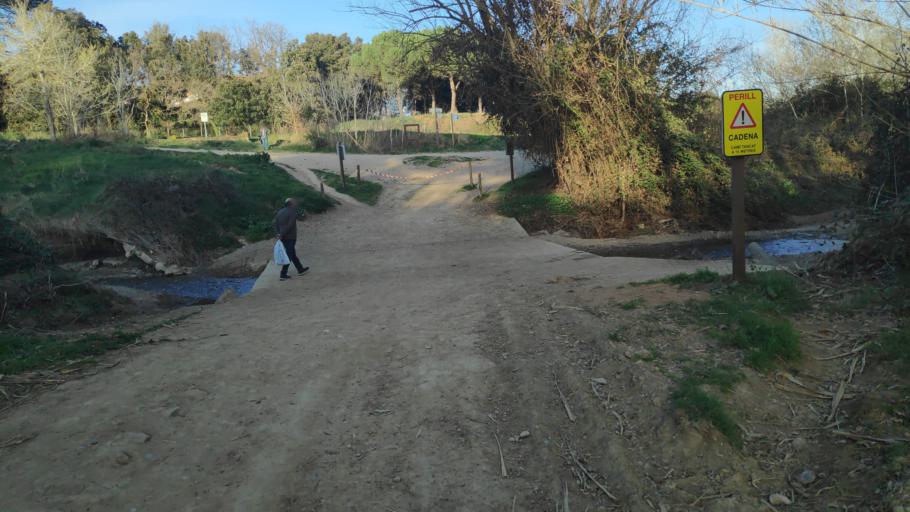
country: ES
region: Catalonia
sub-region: Provincia de Barcelona
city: Sant Quirze del Valles
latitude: 41.5335
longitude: 2.0669
